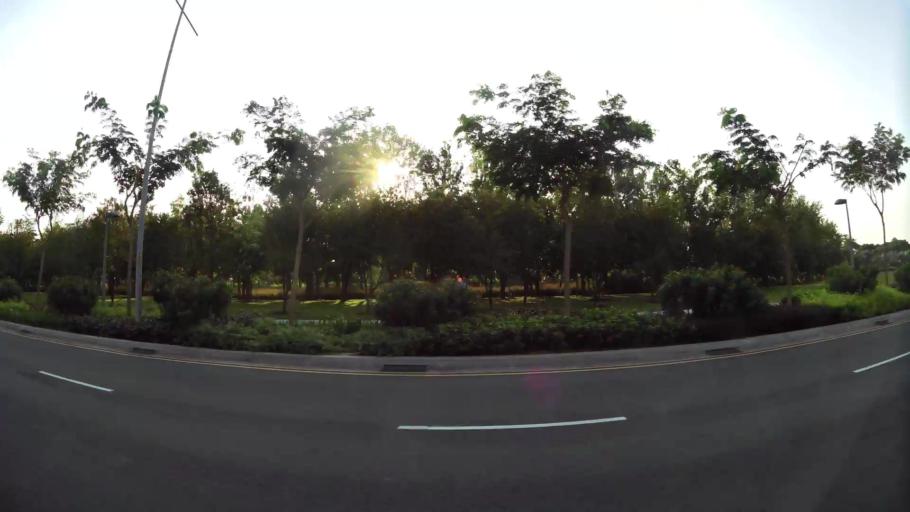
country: SG
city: Singapore
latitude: 1.2793
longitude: 103.8594
